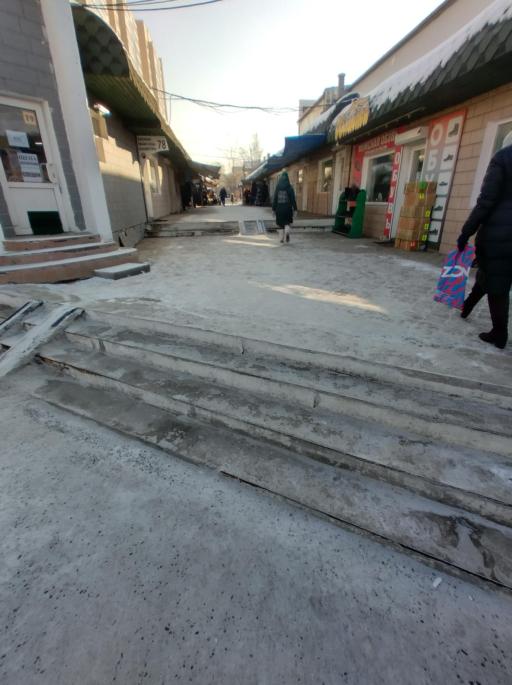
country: RU
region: Transbaikal Territory
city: Chita
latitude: 52.0385
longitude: 113.4953
